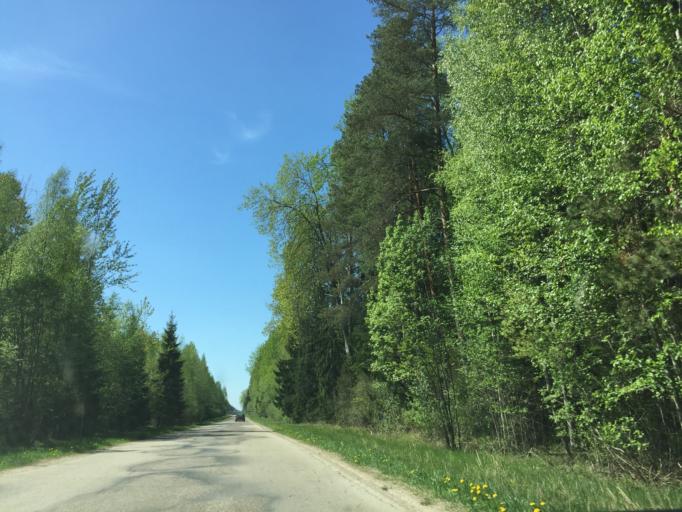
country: LV
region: Ogre
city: Ogre
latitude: 56.8517
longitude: 24.6886
